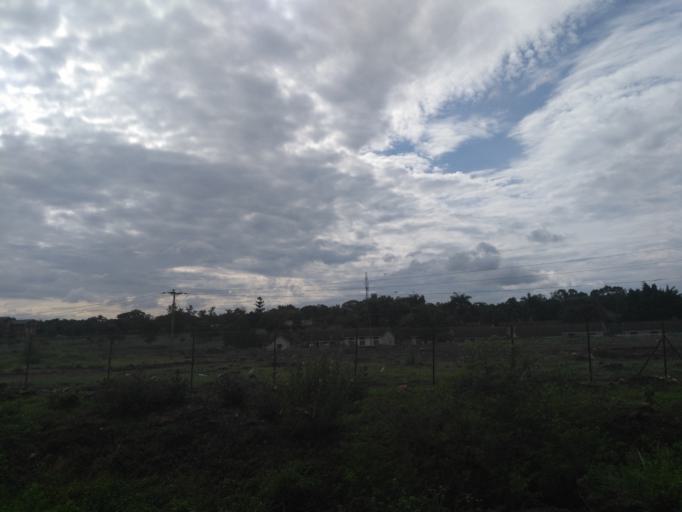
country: UG
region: Eastern Region
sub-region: Jinja District
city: Jinja
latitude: 0.4436
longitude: 33.1949
